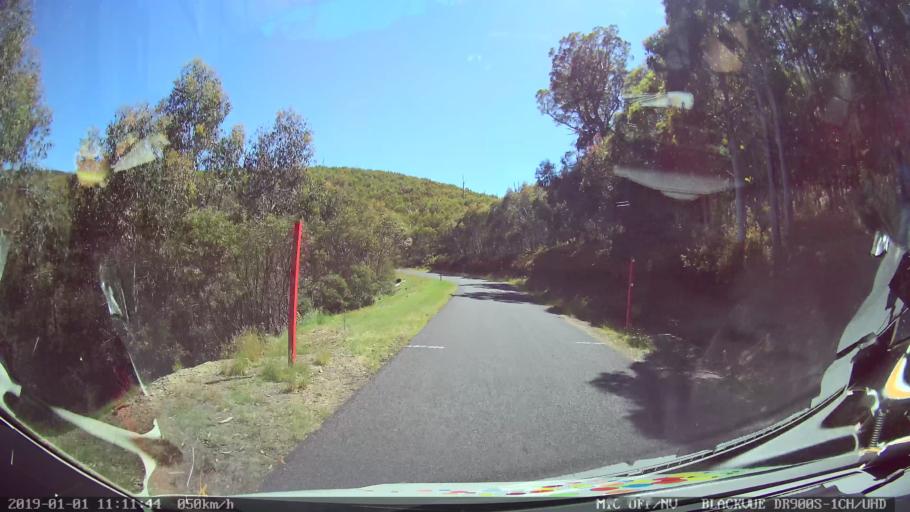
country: AU
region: New South Wales
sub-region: Snowy River
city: Jindabyne
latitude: -35.9602
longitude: 148.4017
